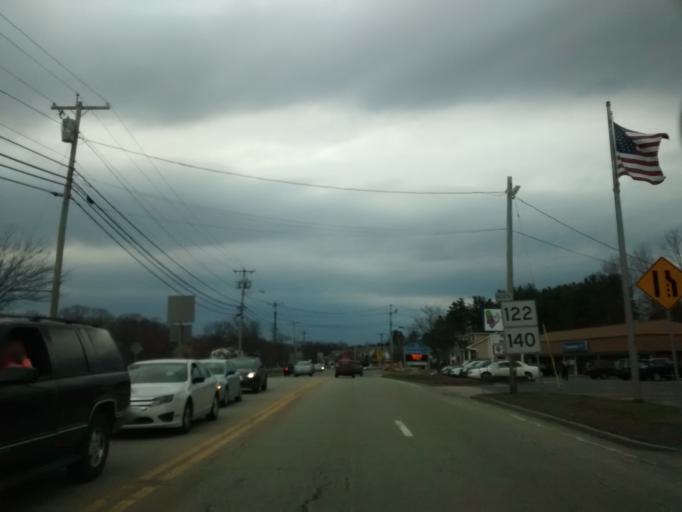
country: US
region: Massachusetts
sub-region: Worcester County
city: Grafton
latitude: 42.2142
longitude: -71.6910
